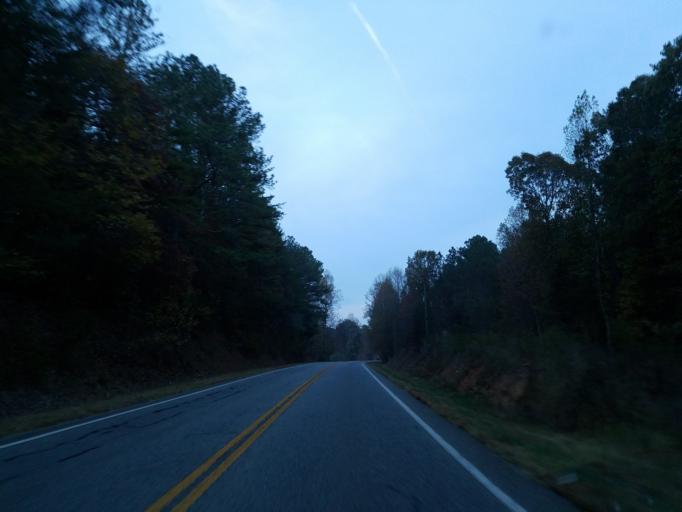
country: US
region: Georgia
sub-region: Gilmer County
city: Ellijay
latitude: 34.5575
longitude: -84.6040
